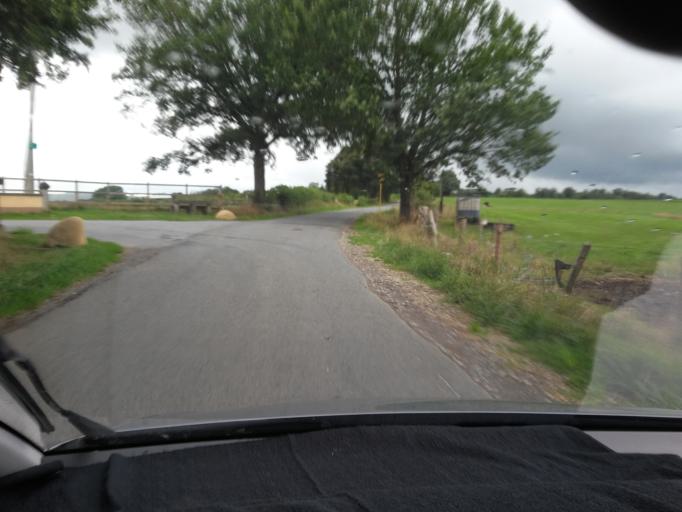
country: BE
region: Wallonia
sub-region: Province du Luxembourg
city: Attert
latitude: 49.7458
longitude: 5.8127
